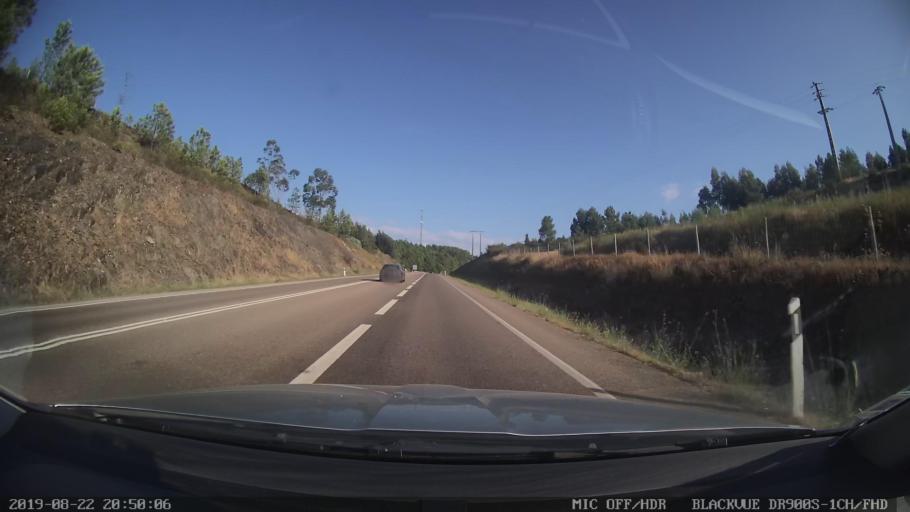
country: PT
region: Castelo Branco
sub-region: Proenca-A-Nova
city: Proenca-a-Nova
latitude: 39.7507
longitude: -7.9359
